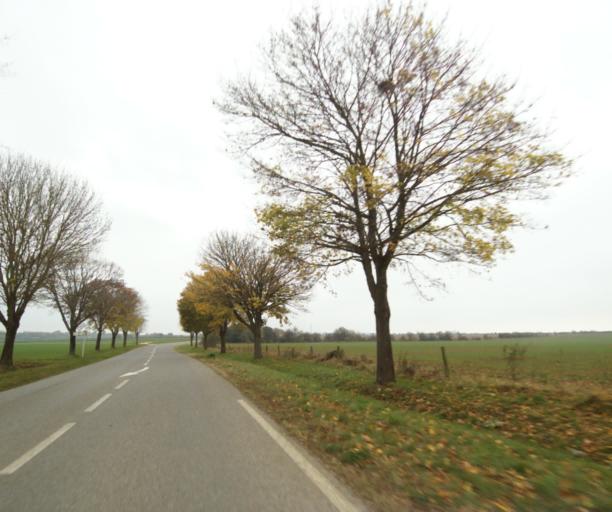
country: FR
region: Lorraine
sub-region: Departement de Meurthe-et-Moselle
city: Moutiers
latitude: 49.2497
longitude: 5.9656
